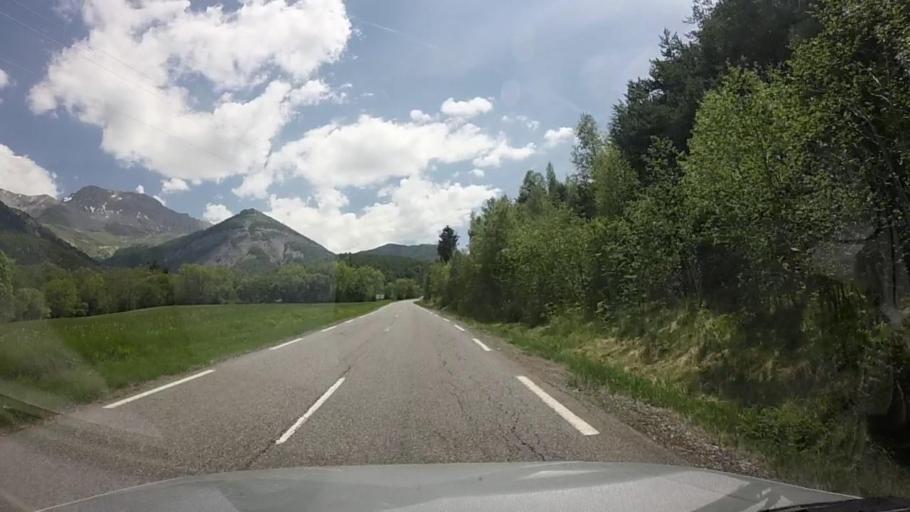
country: FR
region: Provence-Alpes-Cote d'Azur
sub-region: Departement des Alpes-de-Haute-Provence
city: Seyne-les-Alpes
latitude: 44.3224
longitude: 6.3989
